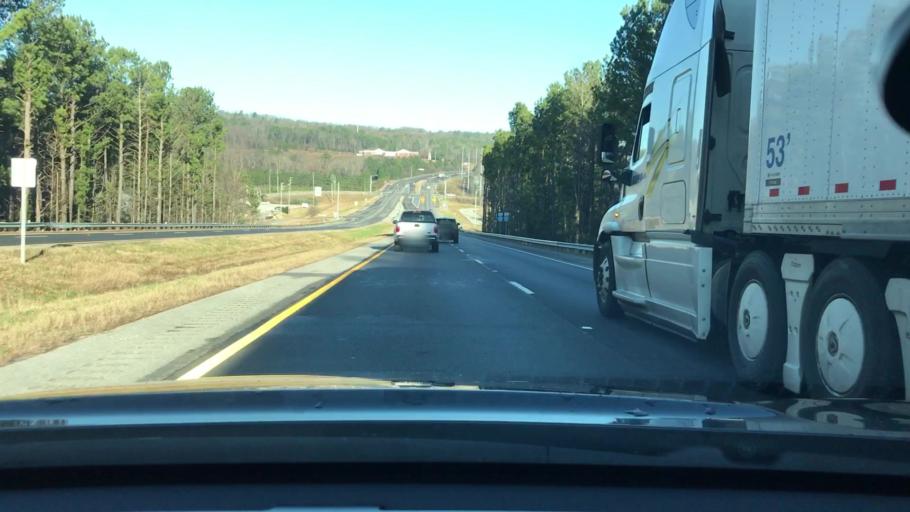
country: US
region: Alabama
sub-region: Shelby County
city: Chelsea
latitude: 33.3679
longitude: -86.6613
